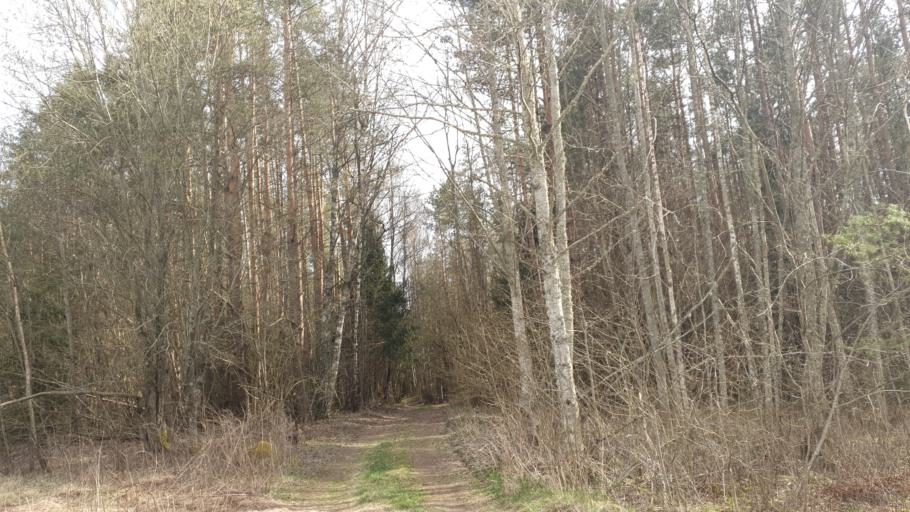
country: LT
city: Aukstadvaris
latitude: 54.5156
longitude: 24.6454
